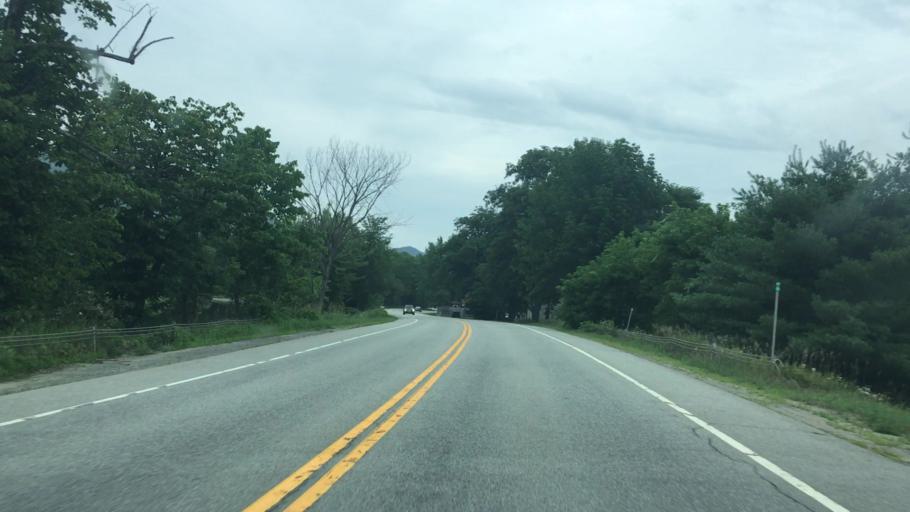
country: US
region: New York
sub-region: Essex County
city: Lake Placid
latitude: 44.3248
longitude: -73.7756
